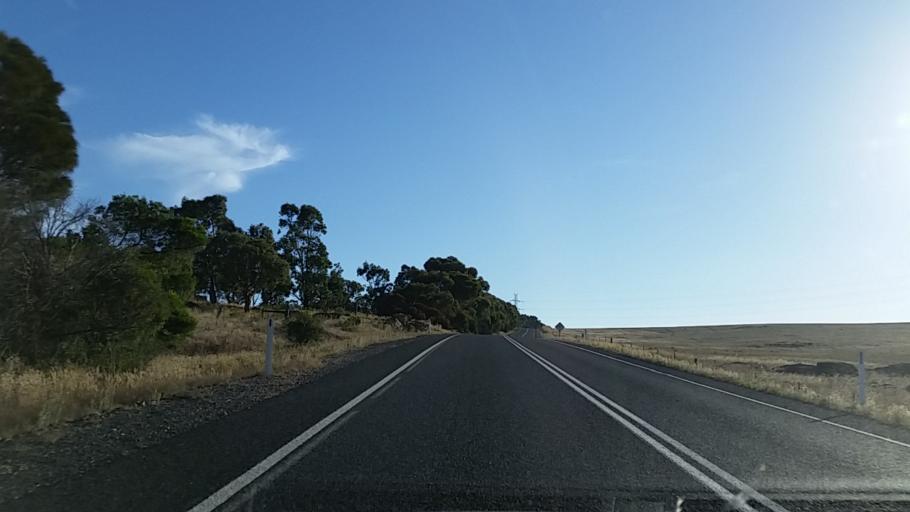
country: AU
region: South Australia
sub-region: Adelaide Hills
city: Birdwood
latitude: -34.7719
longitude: 139.1337
